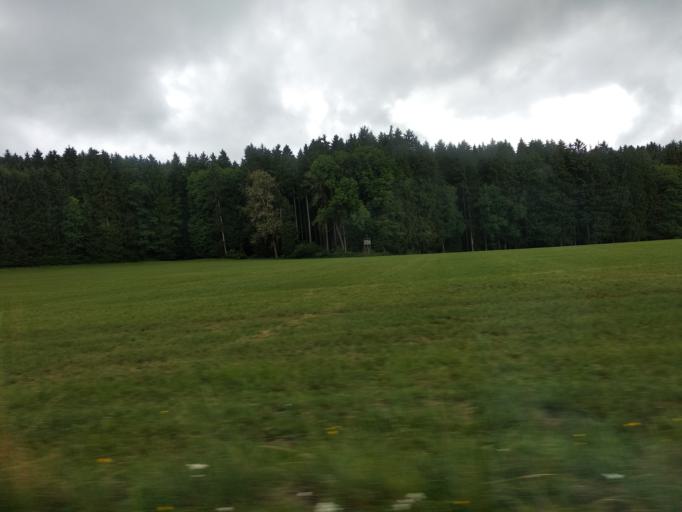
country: DE
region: Bavaria
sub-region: Swabia
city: Wald
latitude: 47.9888
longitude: 10.3161
